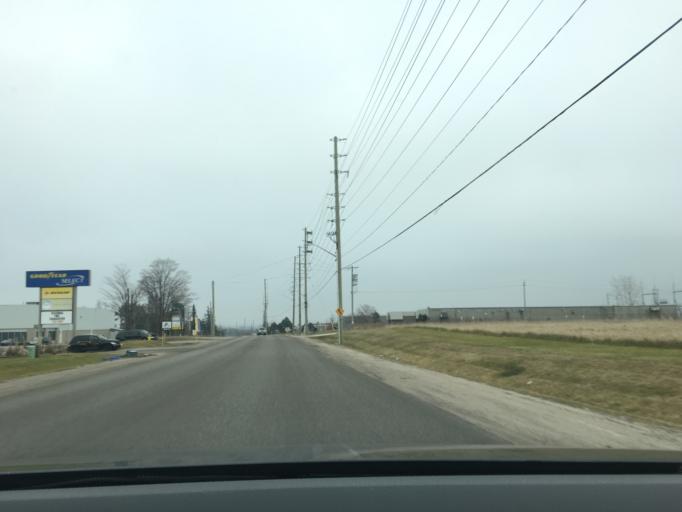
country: CA
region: Ontario
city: Innisfil
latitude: 44.3437
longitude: -79.6763
